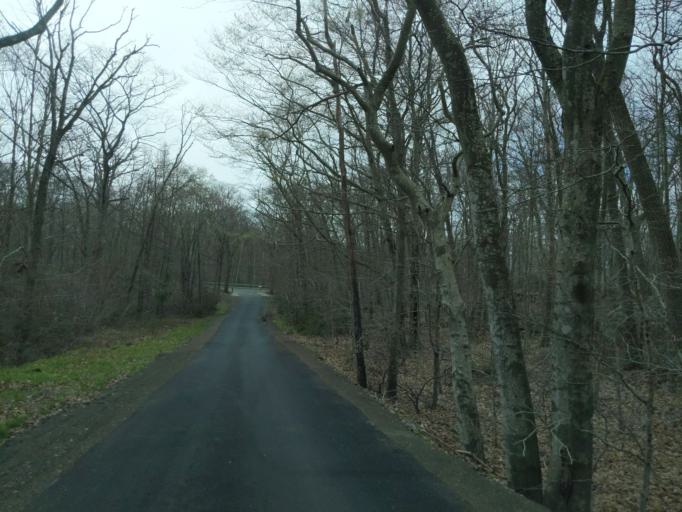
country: US
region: Massachusetts
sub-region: Essex County
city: Rockport
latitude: 42.6400
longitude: -70.6056
